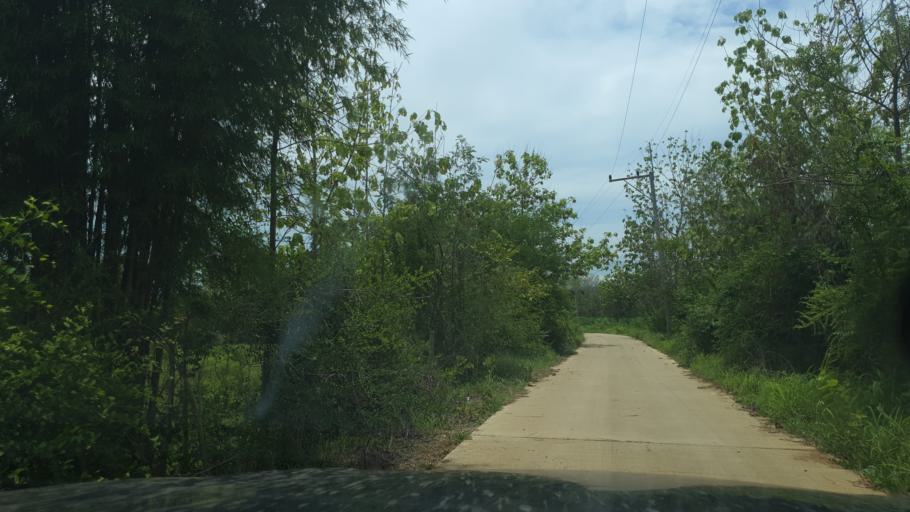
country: TH
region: Lampang
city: Ko Kha
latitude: 18.1307
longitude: 99.3361
